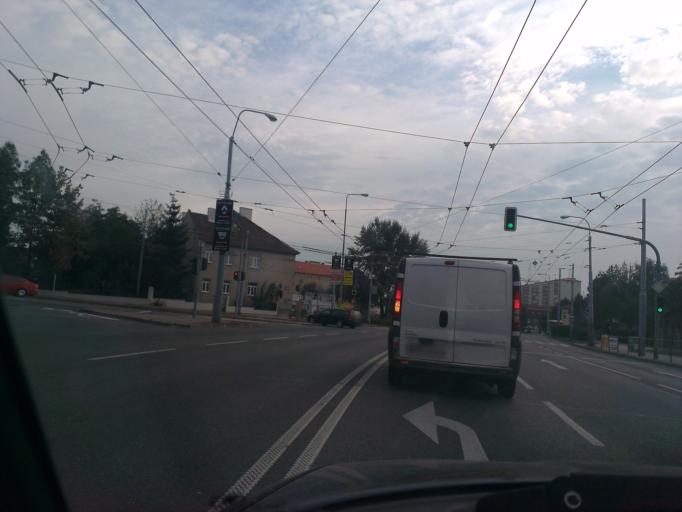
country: CZ
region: South Moravian
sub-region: Mesto Brno
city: Brno
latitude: 49.2061
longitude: 16.6420
